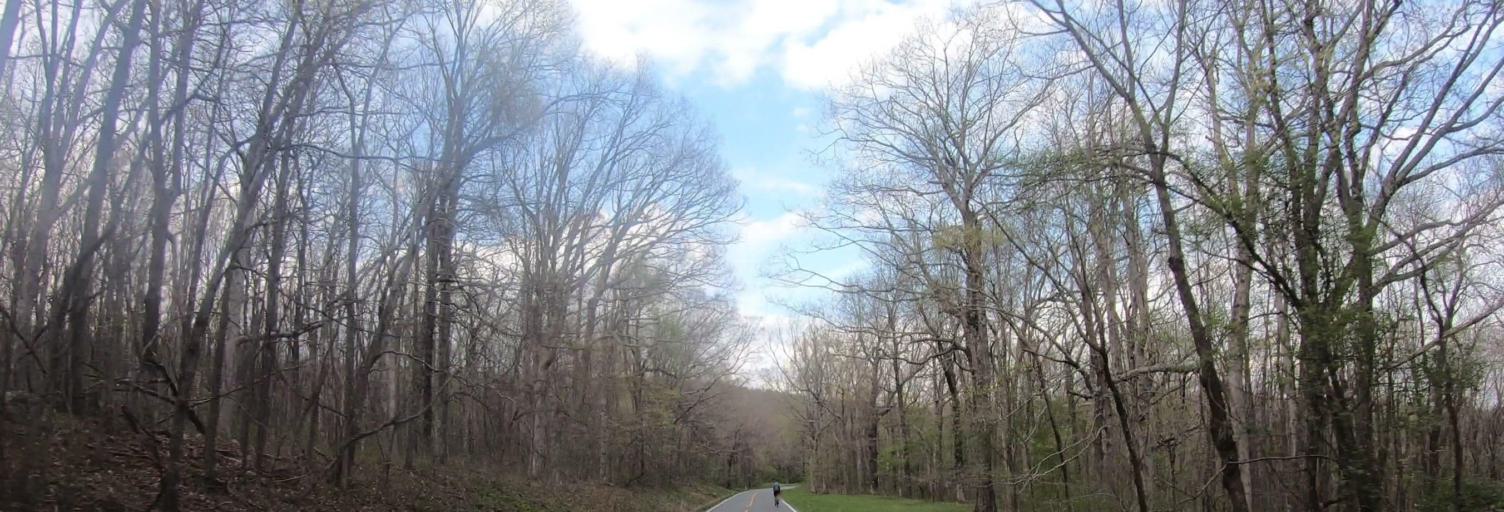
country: US
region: Virginia
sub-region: Augusta County
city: Dooms
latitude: 38.0597
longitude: -78.8059
